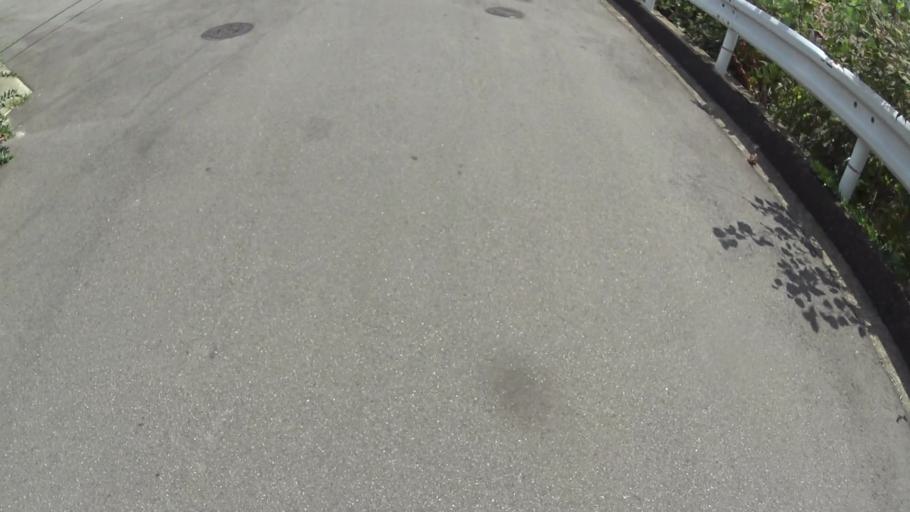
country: JP
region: Kyoto
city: Yawata
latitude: 34.9065
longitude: 135.6950
